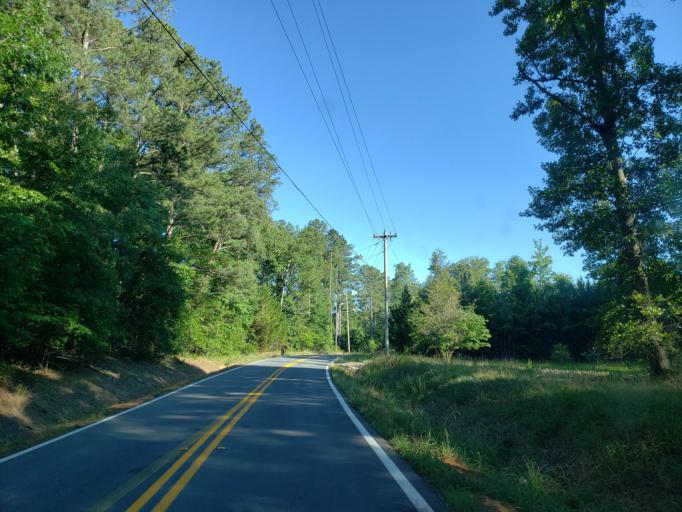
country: US
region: Georgia
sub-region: Floyd County
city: Shannon
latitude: 34.4630
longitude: -85.1158
